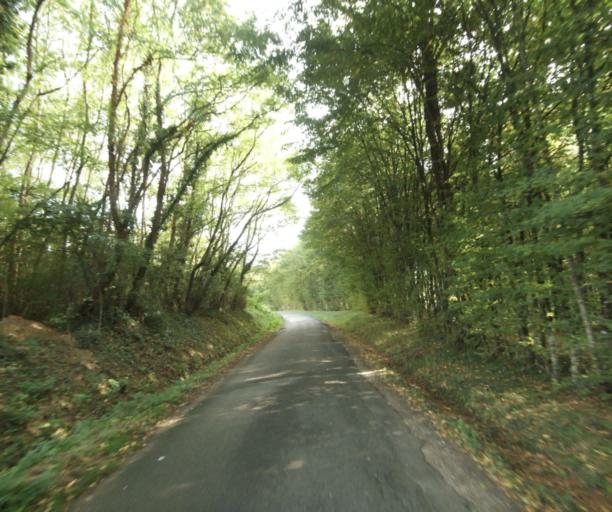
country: FR
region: Midi-Pyrenees
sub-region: Departement du Gers
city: Eauze
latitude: 43.8824
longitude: 0.1066
